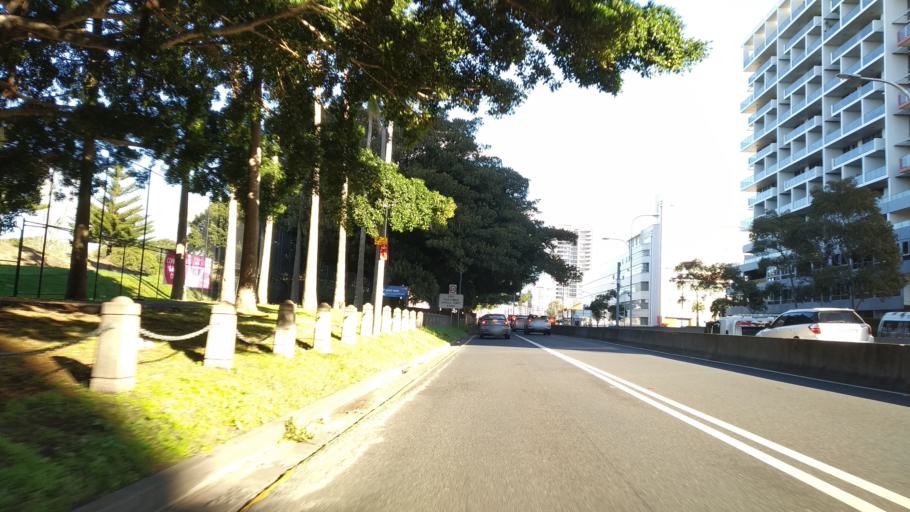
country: AU
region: New South Wales
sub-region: City of Sydney
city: Redfern
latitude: -33.8986
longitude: 151.2156
